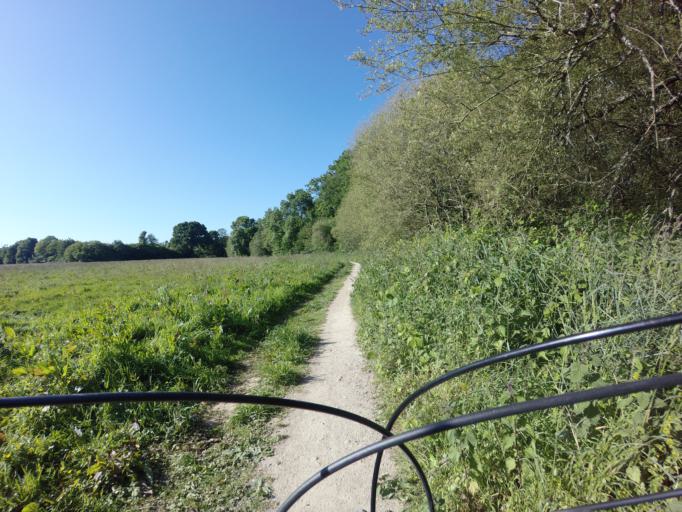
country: FR
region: Brittany
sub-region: Departement du Finistere
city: Quimper
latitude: 48.0129
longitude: -4.1158
